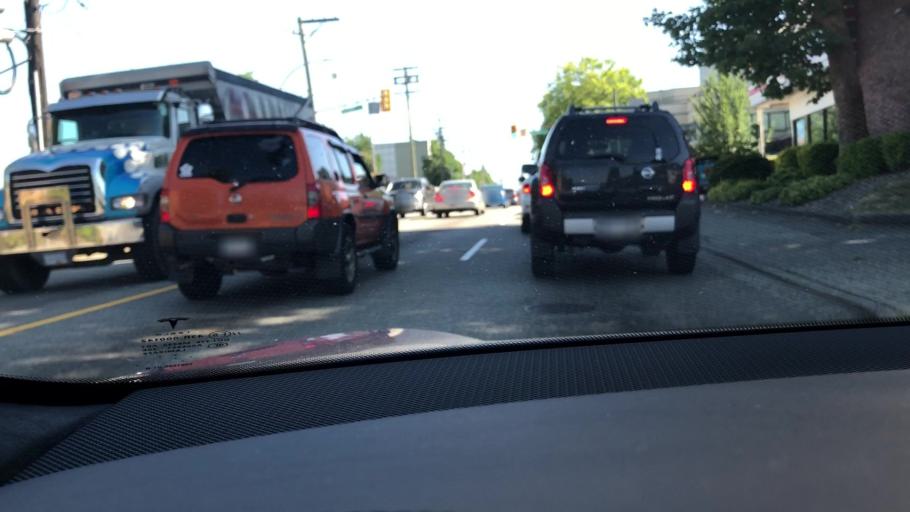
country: CA
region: British Columbia
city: Burnaby
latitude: 49.2255
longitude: -122.9890
